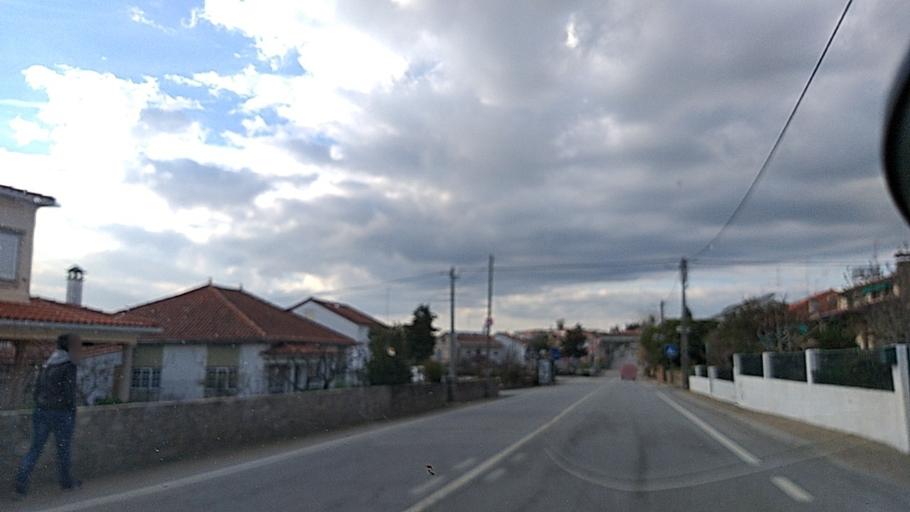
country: ES
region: Castille and Leon
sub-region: Provincia de Salamanca
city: Aldea del Obispo
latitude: 40.7194
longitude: -6.9015
